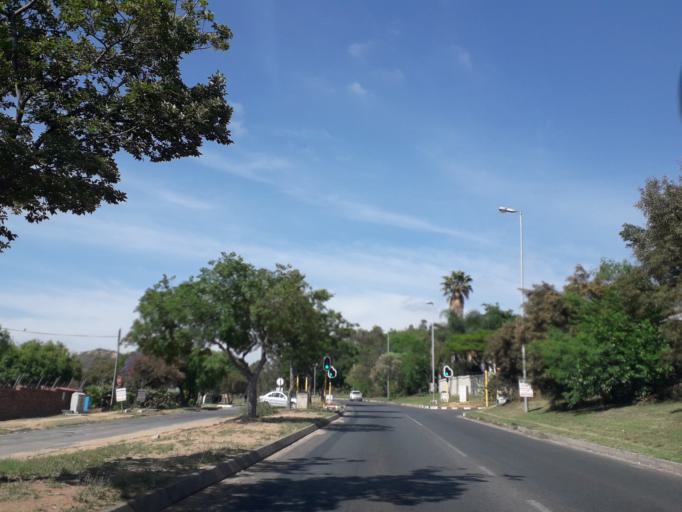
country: ZA
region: Gauteng
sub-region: City of Johannesburg Metropolitan Municipality
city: Roodepoort
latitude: -26.0755
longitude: 27.9606
